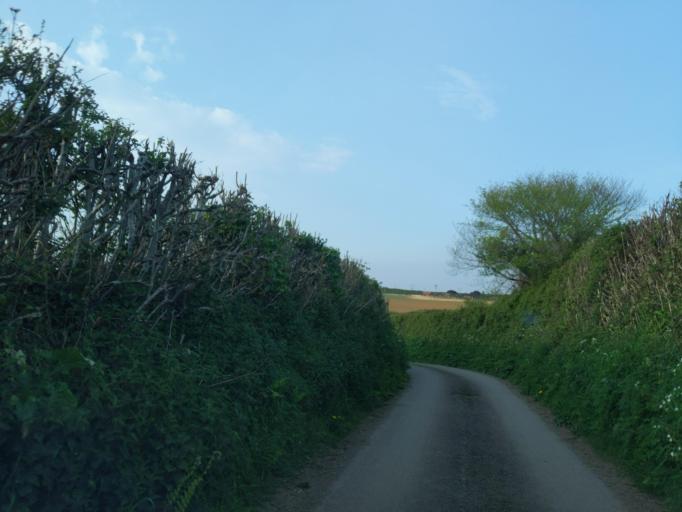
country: GB
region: England
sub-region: Devon
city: Yealmpton
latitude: 50.3539
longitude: -4.0390
